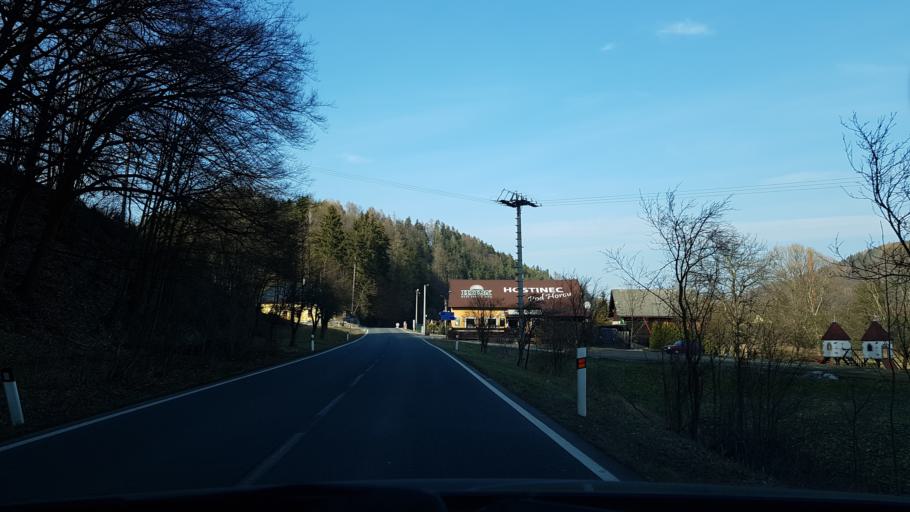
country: CZ
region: Olomoucky
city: Dolni Bohdikov
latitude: 50.0081
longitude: 16.8948
